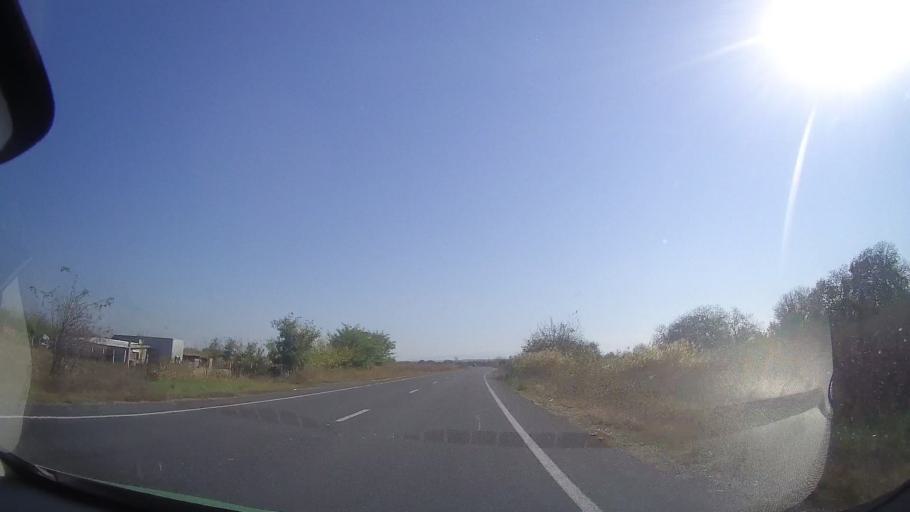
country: RO
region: Timis
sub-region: Comuna Costeiu
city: Costeiu
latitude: 45.7415
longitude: 21.8318
